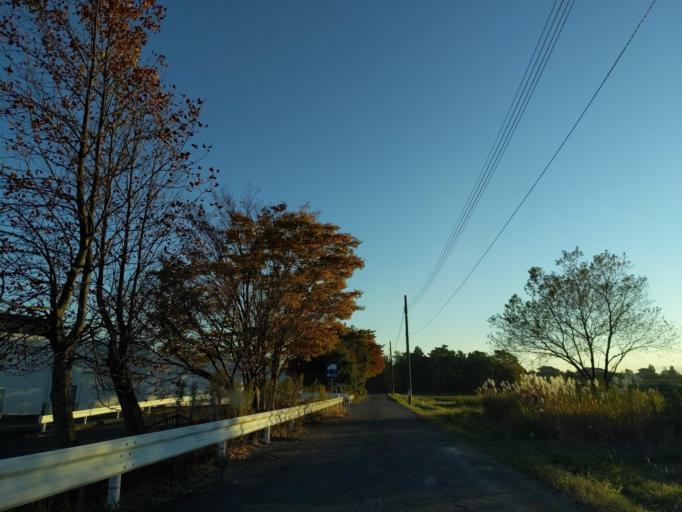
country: JP
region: Fukushima
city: Koriyama
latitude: 37.4431
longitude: 140.3734
